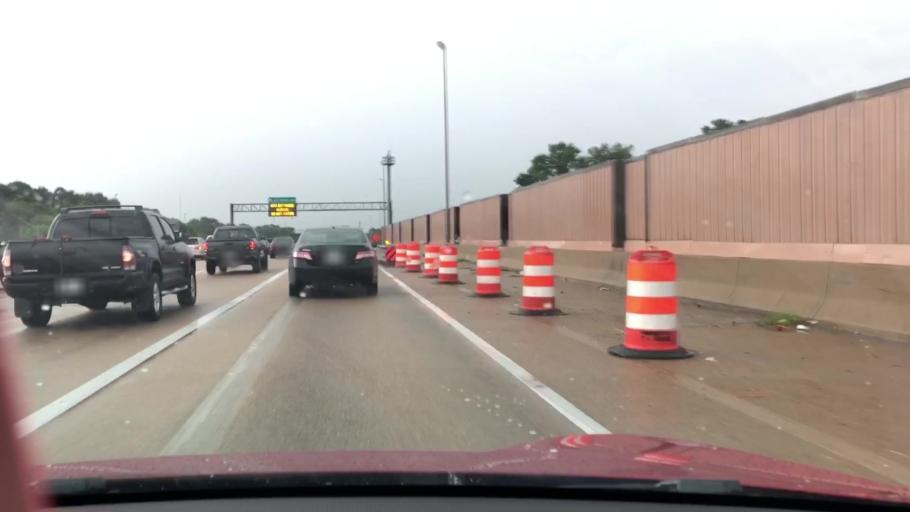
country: US
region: Virginia
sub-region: City of Chesapeake
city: Chesapeake
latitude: 36.8291
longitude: -76.1953
